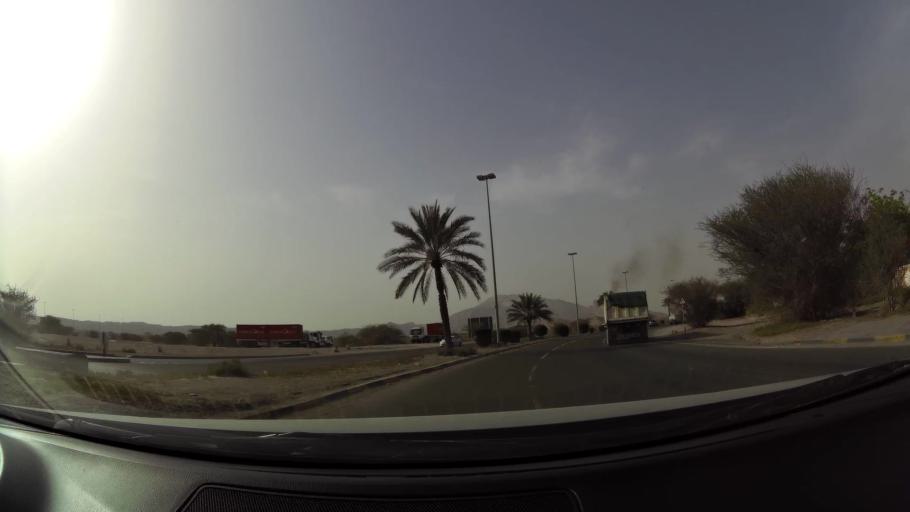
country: AE
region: Abu Dhabi
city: Al Ain
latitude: 24.1389
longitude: 55.7376
